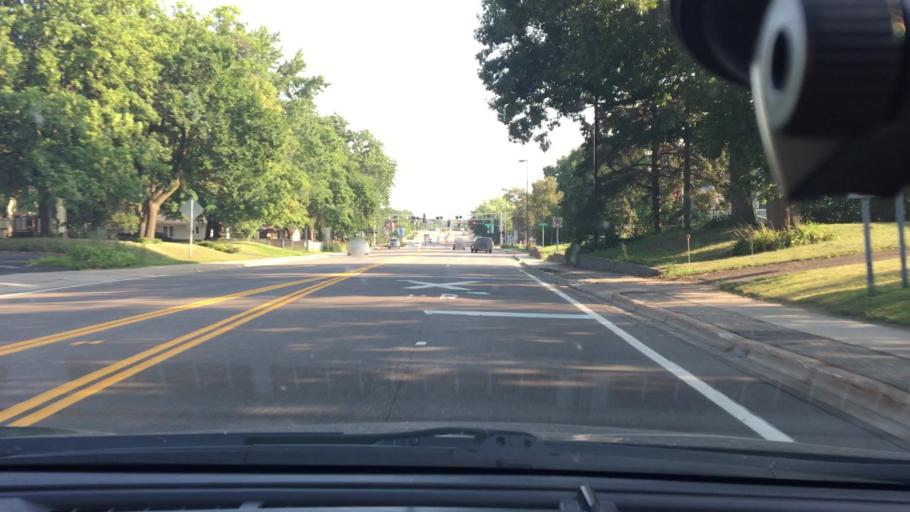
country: US
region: Minnesota
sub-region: Hennepin County
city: Golden Valley
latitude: 44.9909
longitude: -93.3805
